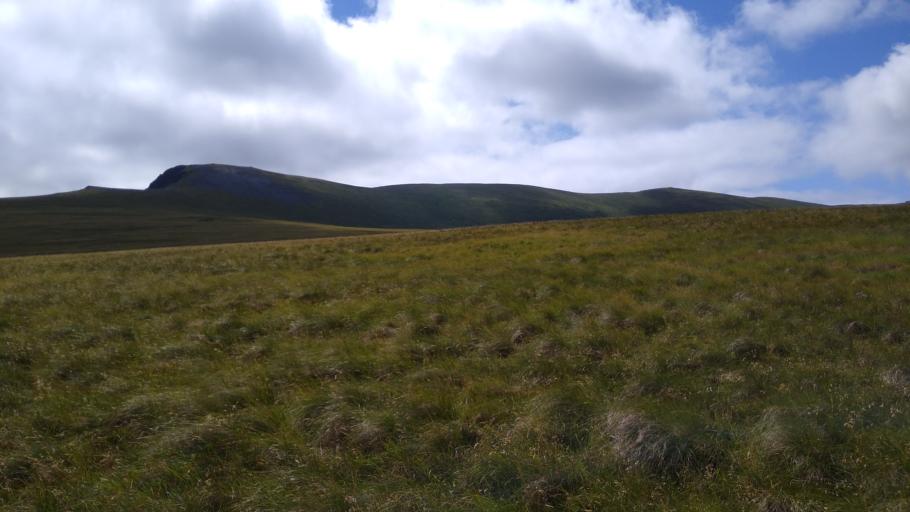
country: GB
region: England
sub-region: Cumbria
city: Keswick
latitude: 54.6537
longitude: -3.0630
